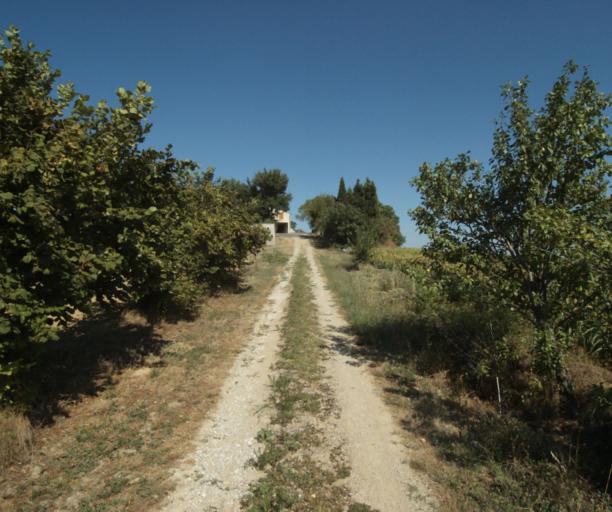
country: FR
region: Midi-Pyrenees
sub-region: Departement de la Haute-Garonne
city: Saint-Felix-Lauragais
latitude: 43.5148
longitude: 1.9379
